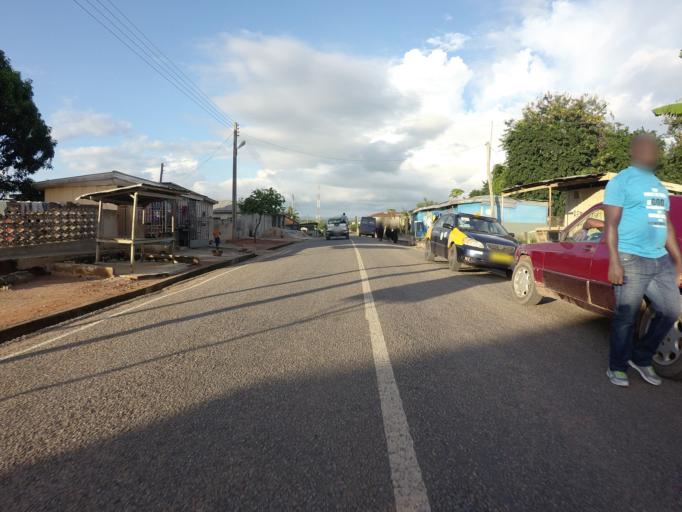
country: GH
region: Ashanti
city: Tafo
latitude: 6.9407
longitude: -1.6781
